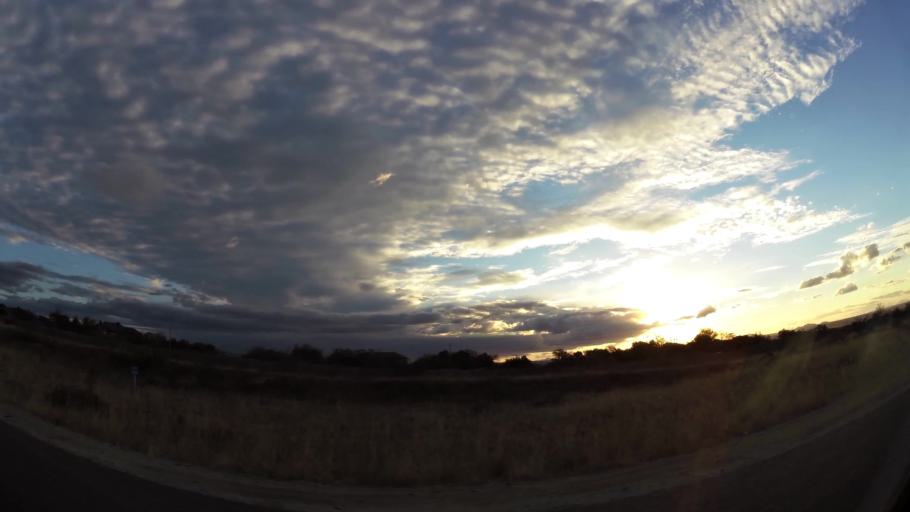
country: ZA
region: Limpopo
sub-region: Capricorn District Municipality
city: Polokwane
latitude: -23.8698
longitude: 29.5069
